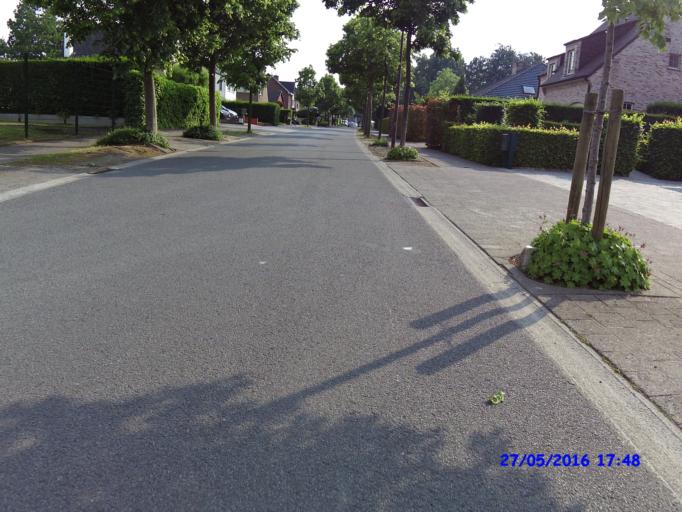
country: BE
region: Flanders
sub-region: Provincie Vlaams-Brabant
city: Asse
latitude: 50.8977
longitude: 4.2397
